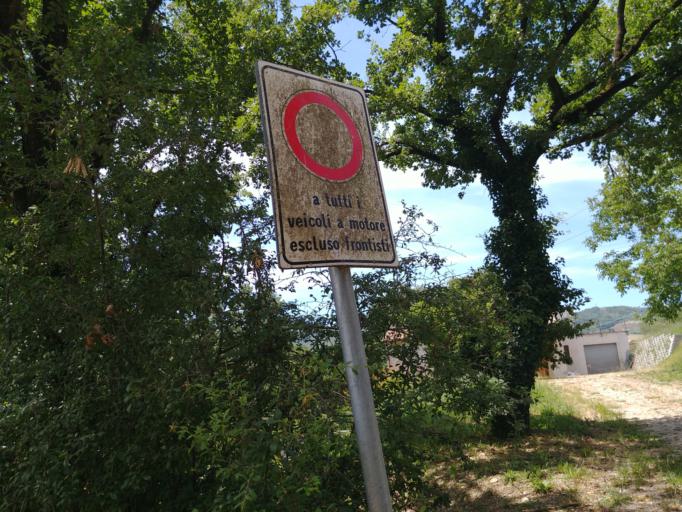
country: IT
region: Umbria
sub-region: Provincia di Perugia
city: Monte Castello di Vibio
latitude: 42.8320
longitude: 12.3720
